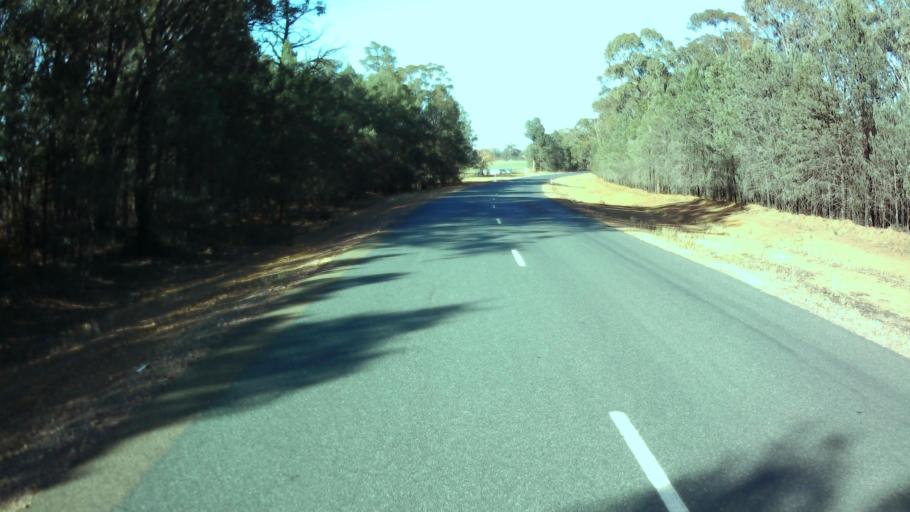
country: AU
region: New South Wales
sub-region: Weddin
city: Grenfell
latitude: -34.0331
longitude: 148.0902
